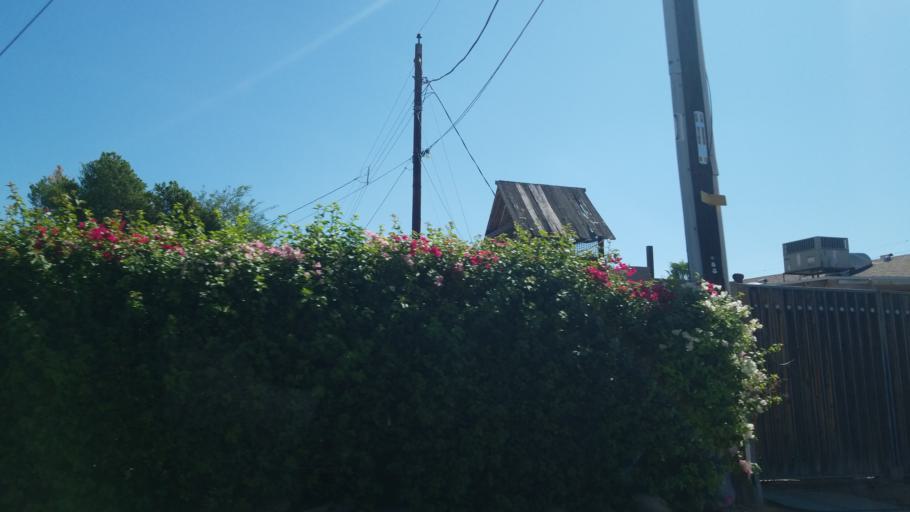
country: US
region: Arizona
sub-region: Maricopa County
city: Scottsdale
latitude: 33.5142
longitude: -111.9001
